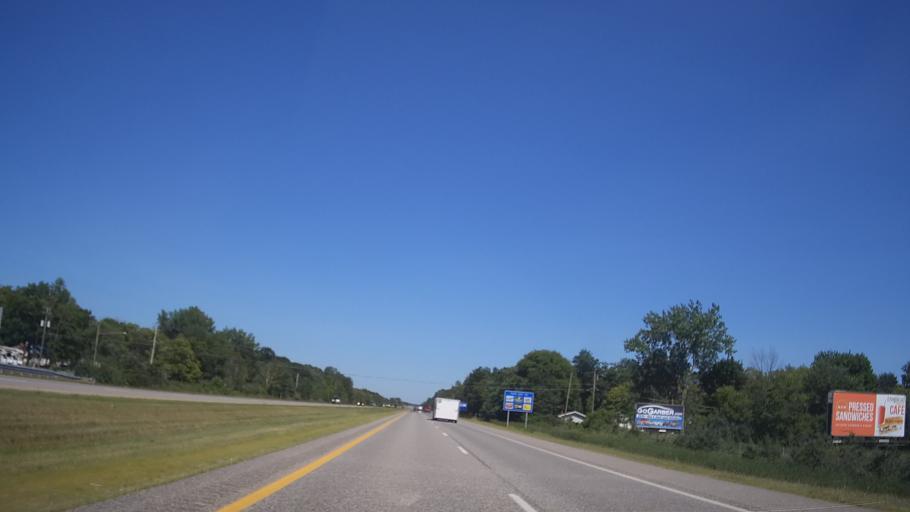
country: US
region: Michigan
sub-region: Midland County
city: Midland
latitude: 43.6561
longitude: -84.2921
